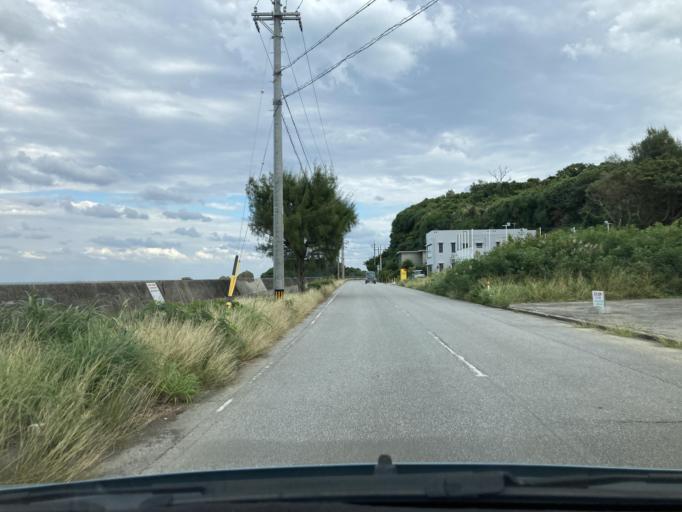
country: JP
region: Okinawa
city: Katsuren-haebaru
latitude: 26.3255
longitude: 127.9615
